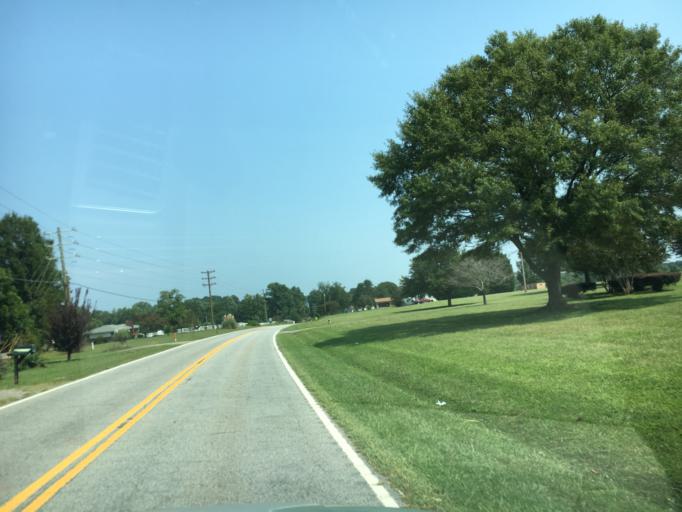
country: US
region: South Carolina
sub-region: Spartanburg County
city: Boiling Springs
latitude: 35.0688
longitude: -81.9318
